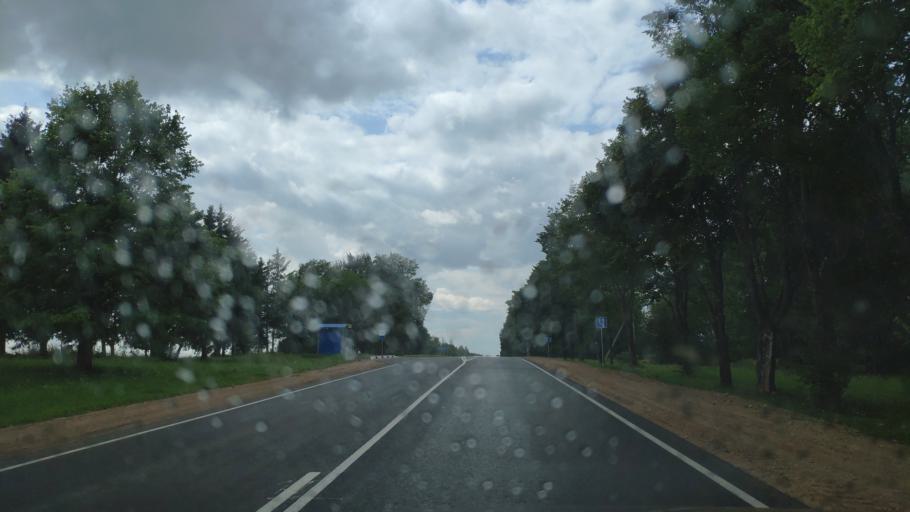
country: BY
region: Minsk
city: Syomkava
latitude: 54.0089
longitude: 27.3991
